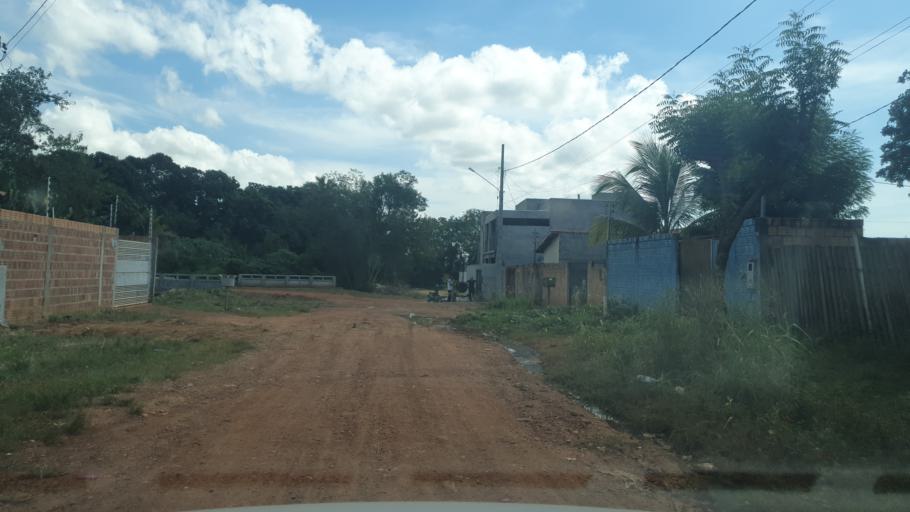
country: BR
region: Mato Grosso
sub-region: Pontes E Lacerda
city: Pontes e Lacerda
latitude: -15.2260
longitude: -59.3442
